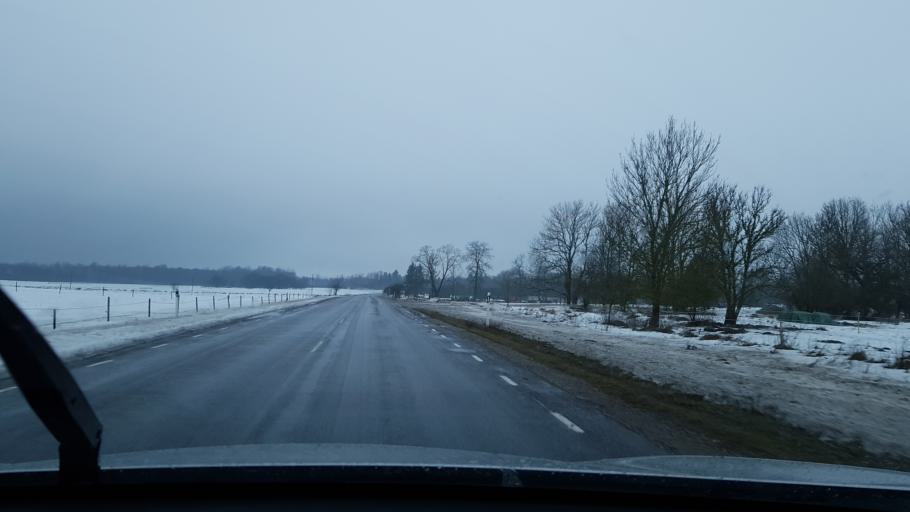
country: EE
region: Harju
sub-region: Nissi vald
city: Turba
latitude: 58.9013
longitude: 24.2223
